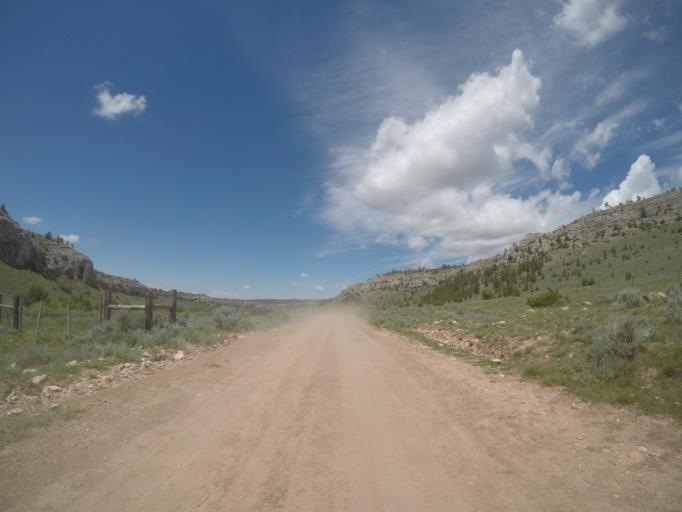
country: US
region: Montana
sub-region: Yellowstone County
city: Laurel
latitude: 45.2357
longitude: -108.6216
